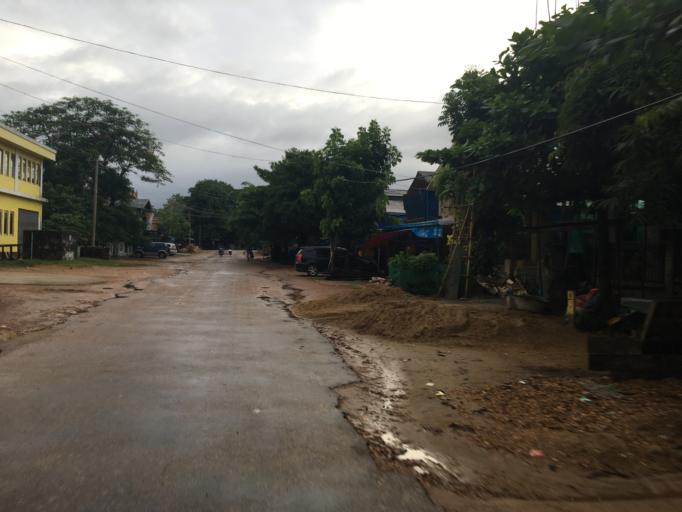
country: MM
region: Mon
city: Mudon
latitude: 16.0406
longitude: 98.1201
